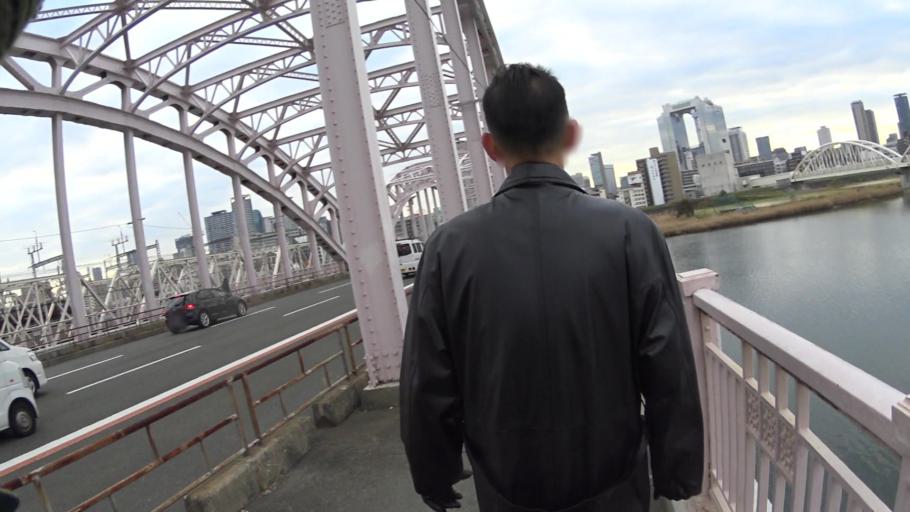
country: JP
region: Osaka
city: Osaka-shi
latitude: 34.7139
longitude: 135.4862
